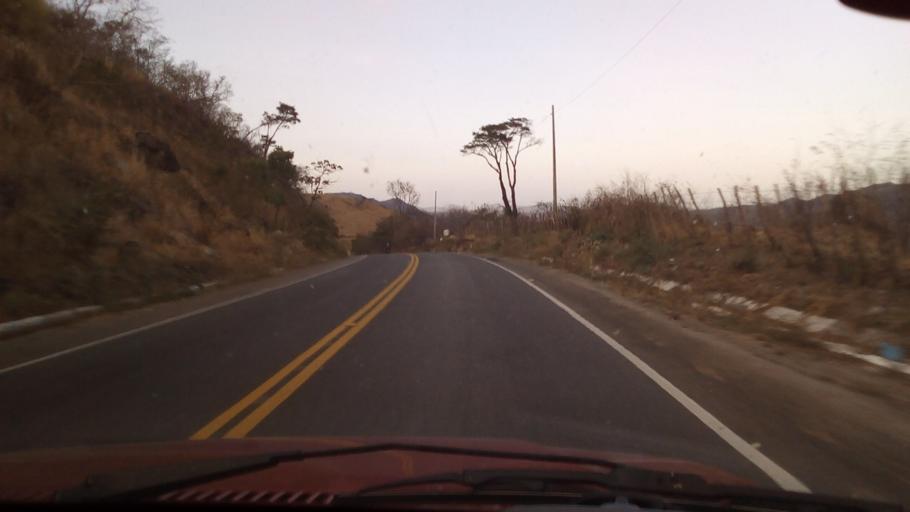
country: BR
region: Paraiba
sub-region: Bananeiras
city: Solanea
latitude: -6.7323
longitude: -35.5550
